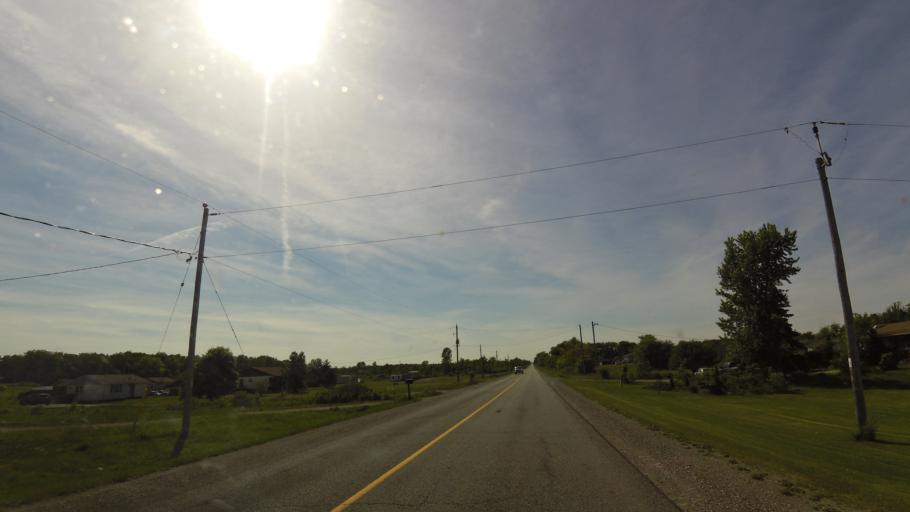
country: CA
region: Ontario
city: Ancaster
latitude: 43.0323
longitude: -80.0188
